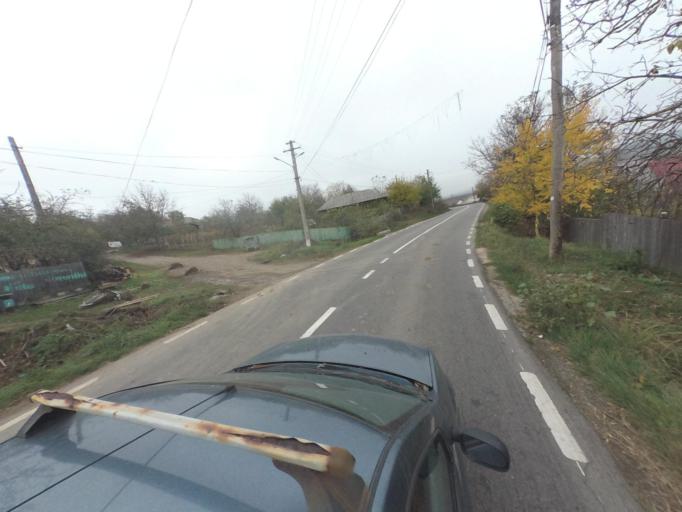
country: RO
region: Vaslui
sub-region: Comuna Bacesti
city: Bacesti
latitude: 46.8278
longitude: 27.2417
